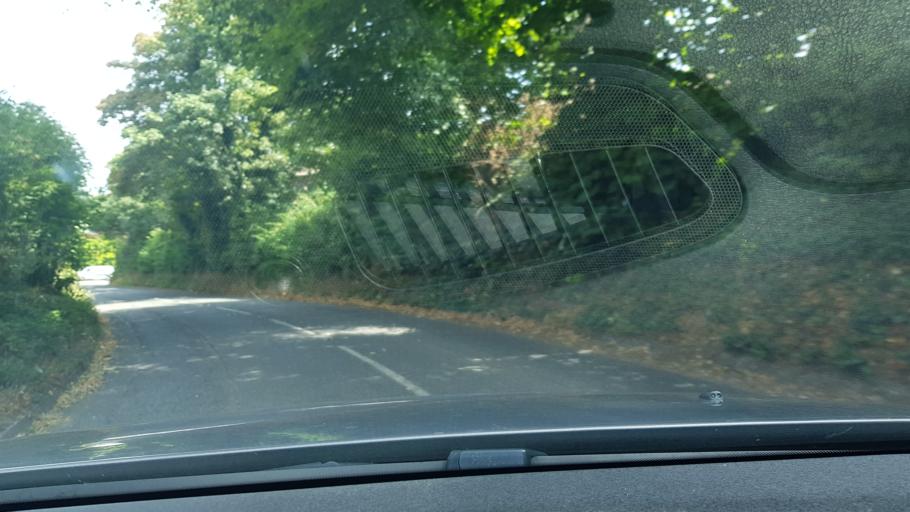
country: GB
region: England
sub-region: West Berkshire
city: Wickham
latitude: 51.4749
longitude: -1.4540
